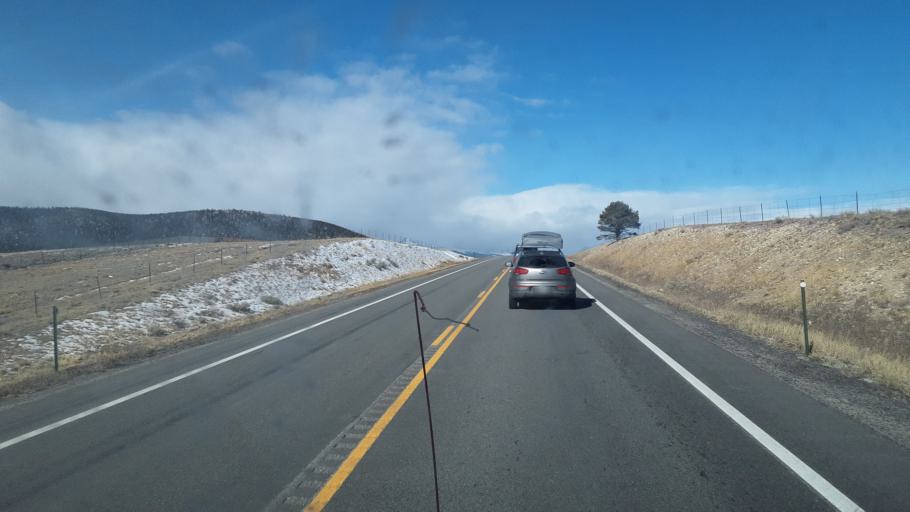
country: US
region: Colorado
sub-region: Park County
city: Fairplay
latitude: 39.0874
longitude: -105.9808
